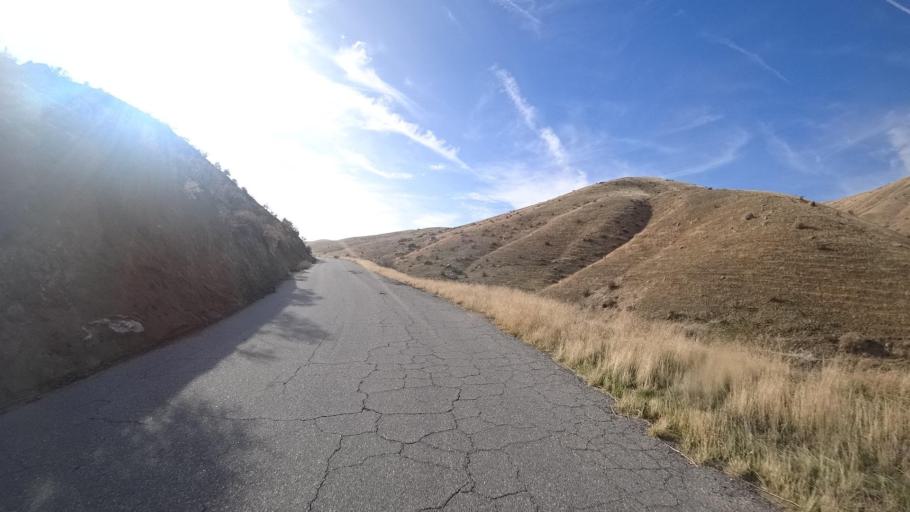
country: US
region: California
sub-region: Kern County
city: Bear Valley Springs
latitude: 35.2874
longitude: -118.6677
